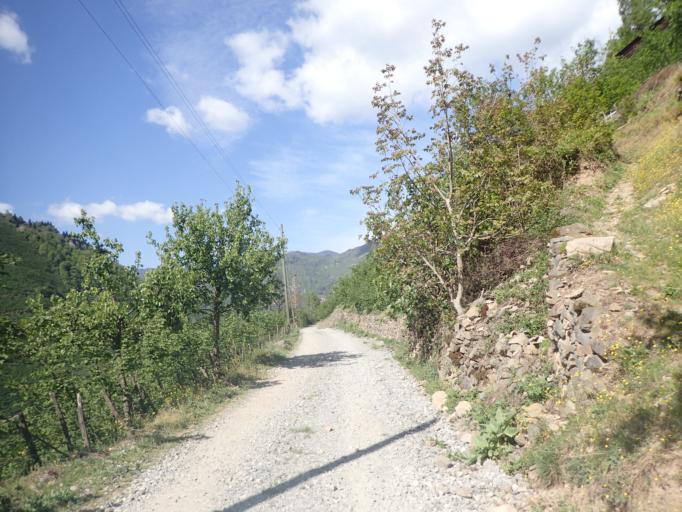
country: TR
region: Ordu
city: Topcam
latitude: 40.7157
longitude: 37.8743
